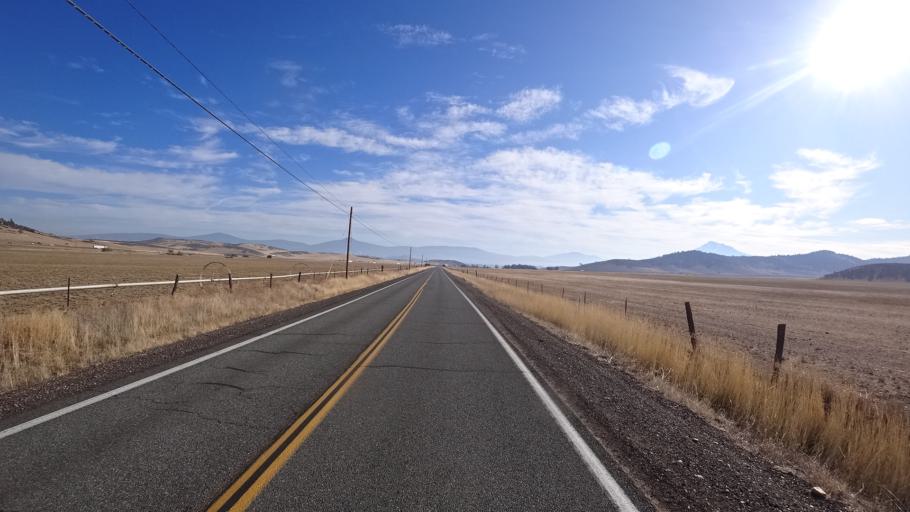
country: US
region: California
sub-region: Siskiyou County
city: Montague
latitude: 41.6546
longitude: -122.5757
